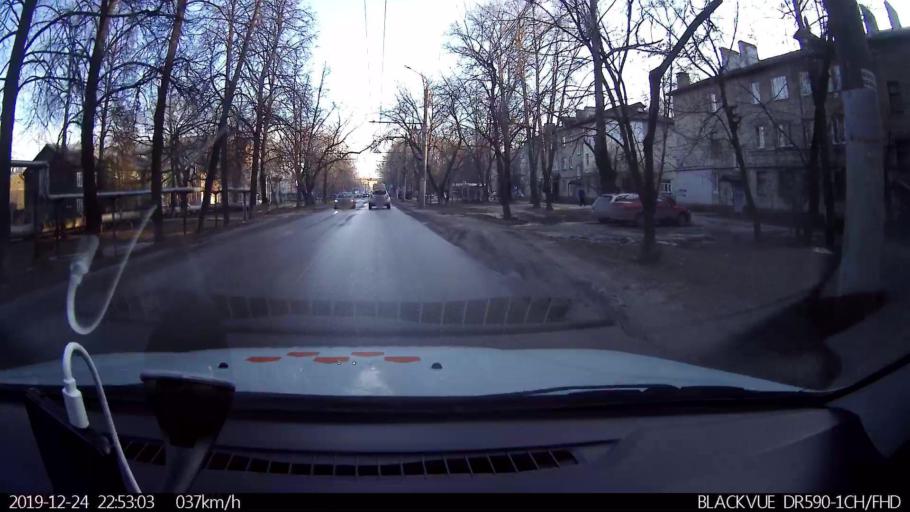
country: RU
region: Nizjnij Novgorod
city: Nizhniy Novgorod
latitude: 56.2857
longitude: 43.9208
